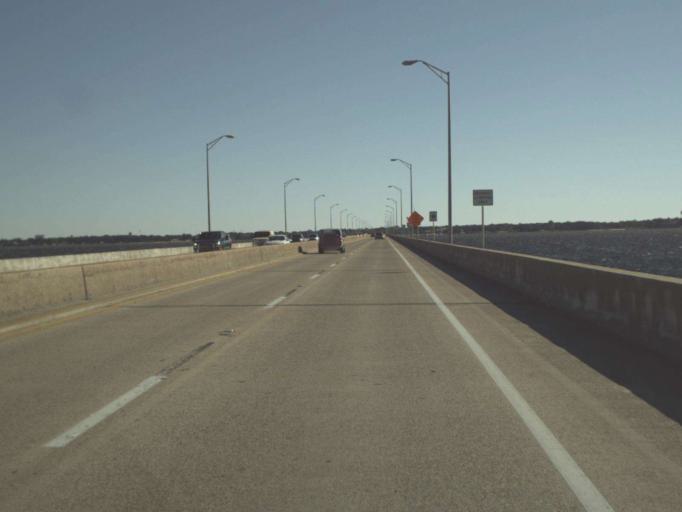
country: US
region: Florida
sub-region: Santa Rosa County
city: Gulf Breeze
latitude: 30.3884
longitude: -87.1828
